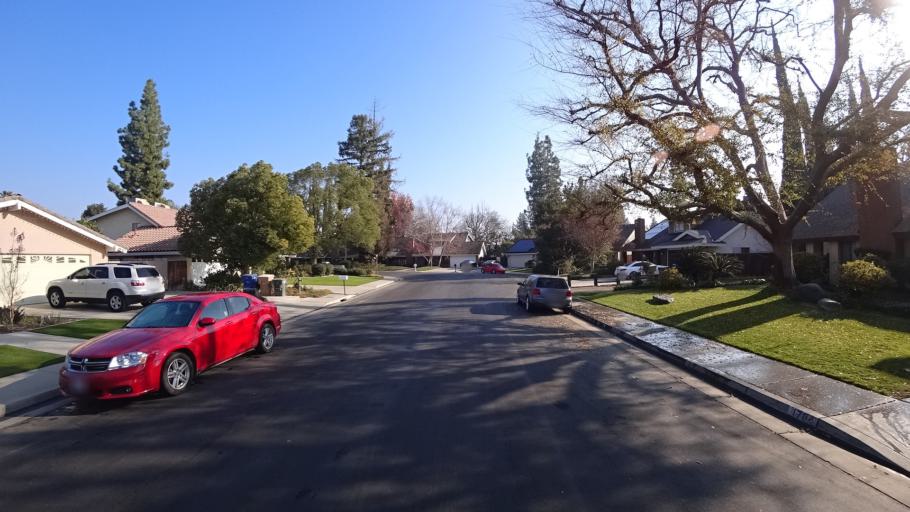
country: US
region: California
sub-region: Kern County
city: Greenacres
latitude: 35.3404
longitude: -119.0720
